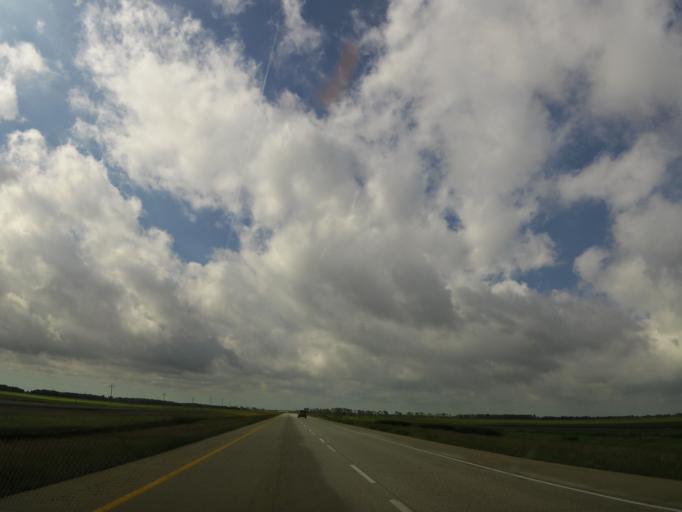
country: US
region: North Dakota
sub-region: Walsh County
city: Grafton
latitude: 48.2586
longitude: -97.1894
